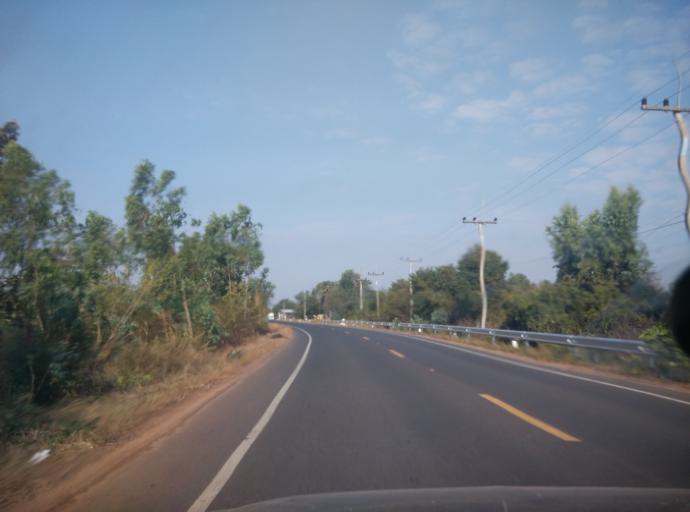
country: TH
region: Sisaket
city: Si Sa Ket
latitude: 15.1135
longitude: 104.2674
